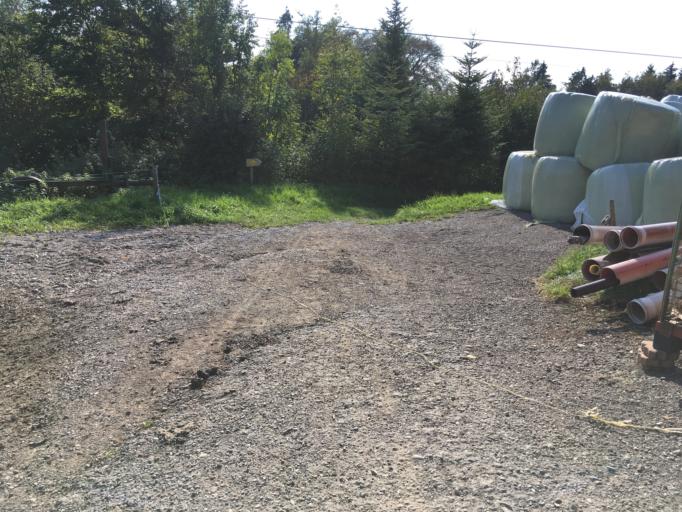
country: CH
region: Zurich
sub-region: Bezirk Hinwil
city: Wetzikon / Kempten
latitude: 47.3436
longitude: 8.8268
